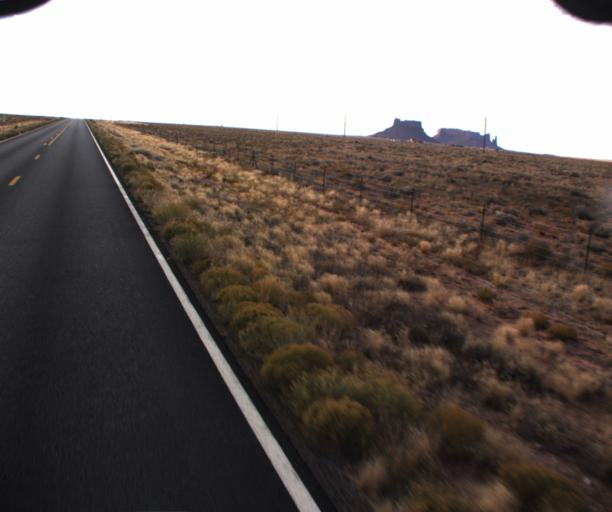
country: US
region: Arizona
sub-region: Apache County
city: Many Farms
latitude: 36.5714
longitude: -109.5481
